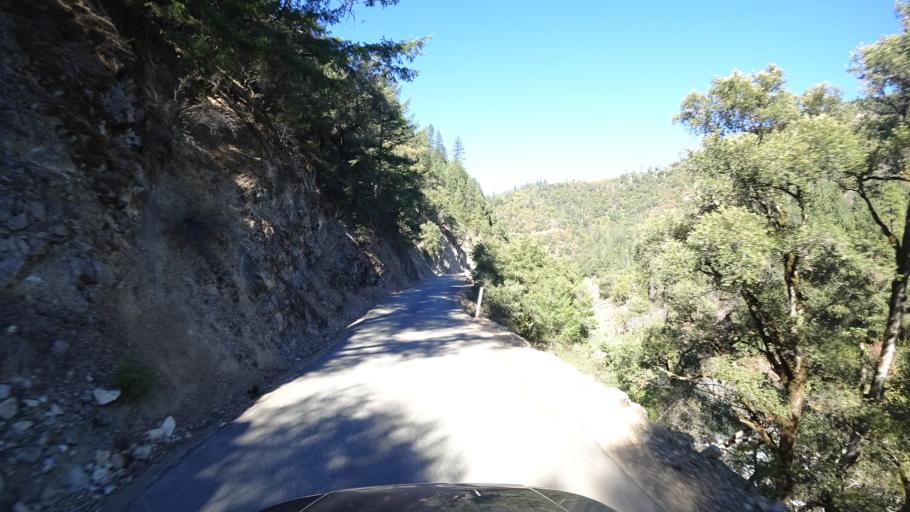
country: US
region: California
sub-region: Humboldt County
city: Willow Creek
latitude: 41.2504
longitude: -123.3057
